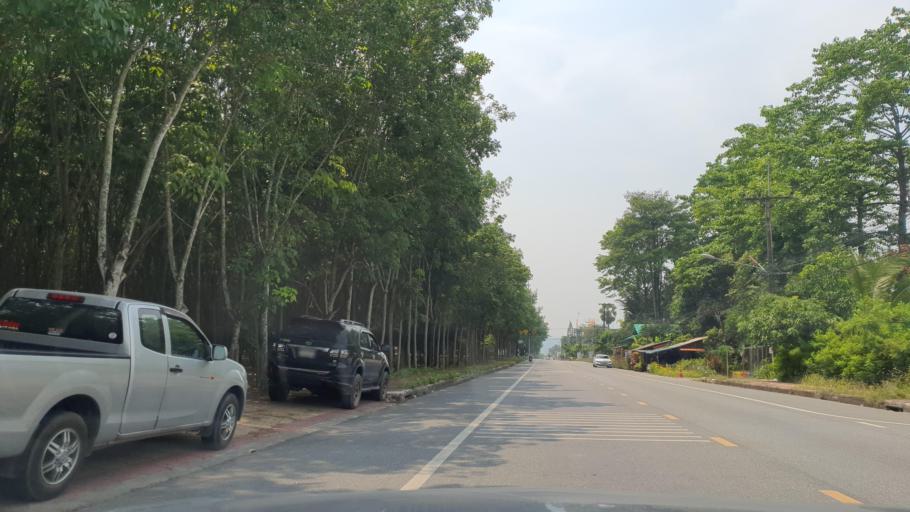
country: TH
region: Rayong
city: Nikhom Phattana
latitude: 12.7875
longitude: 101.1639
